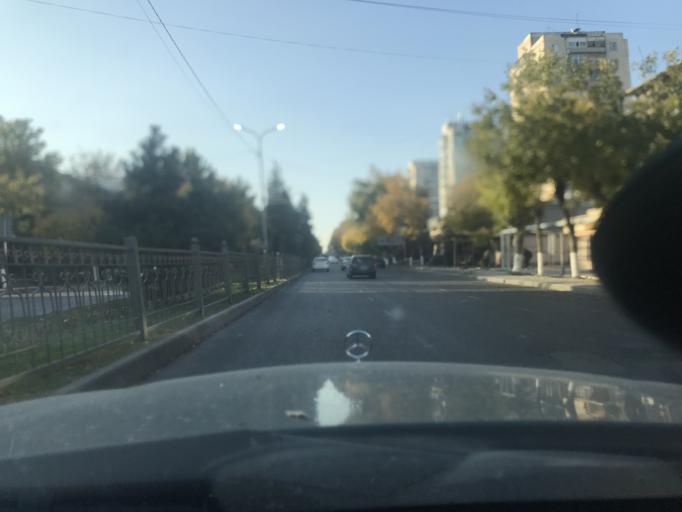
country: KZ
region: Ongtustik Qazaqstan
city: Shymkent
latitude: 42.2997
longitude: 69.6088
